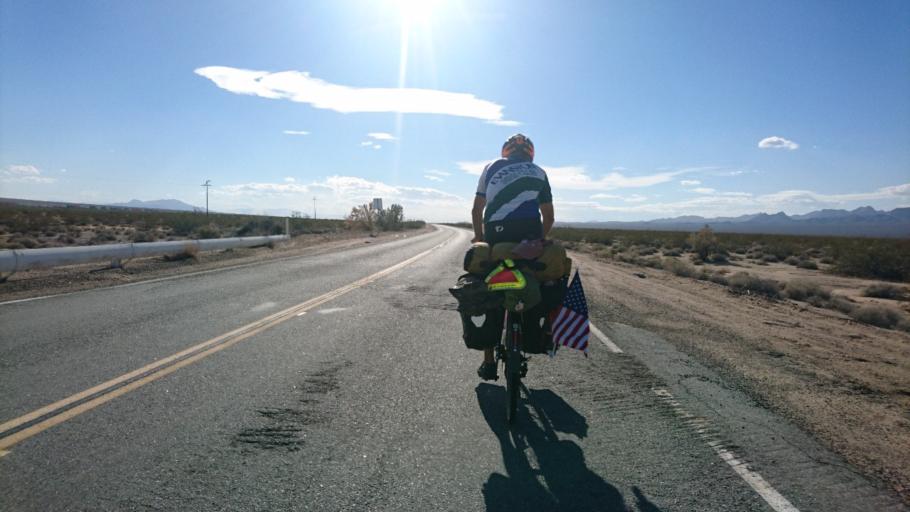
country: US
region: California
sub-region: San Bernardino County
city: Needles
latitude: 34.7273
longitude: -115.2600
